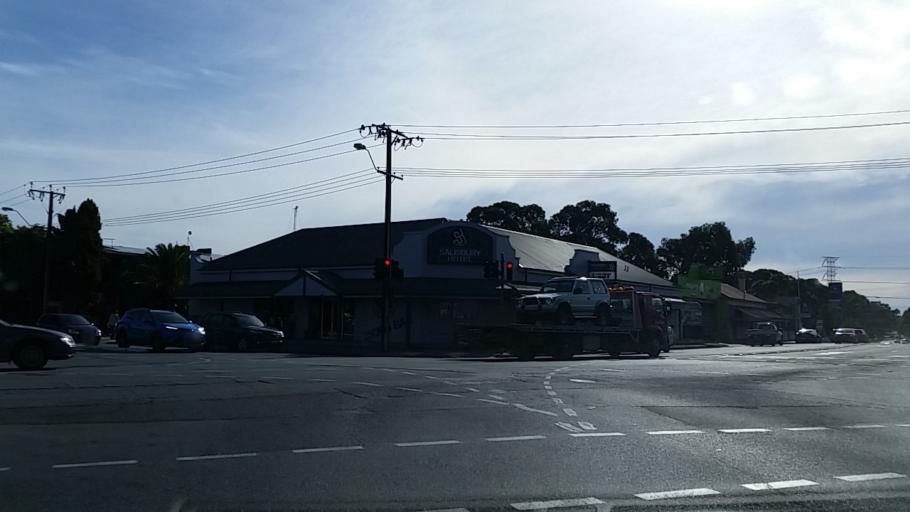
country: AU
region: South Australia
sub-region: Salisbury
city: Salisbury
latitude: -34.7621
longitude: 138.6497
